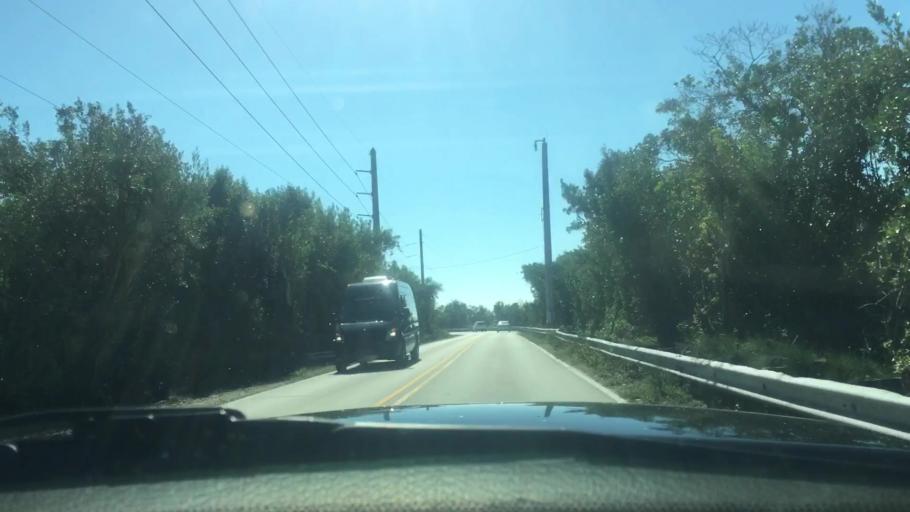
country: US
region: Florida
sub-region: Monroe County
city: North Key Largo
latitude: 25.2983
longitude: -80.3861
